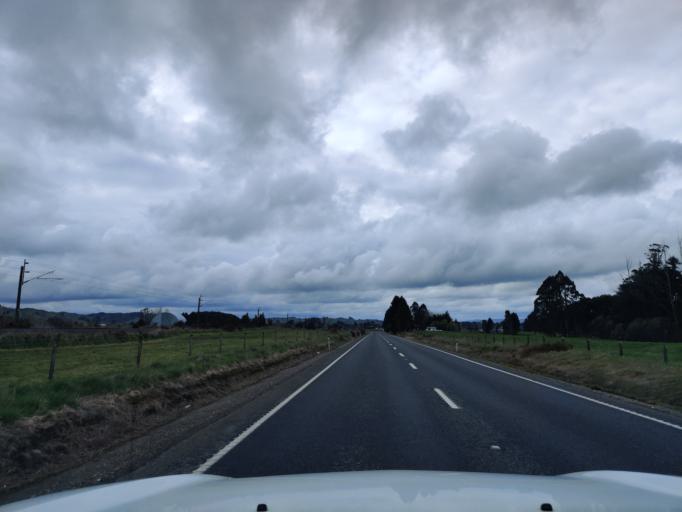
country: NZ
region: Waikato
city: Turangi
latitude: -39.0176
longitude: 175.3789
